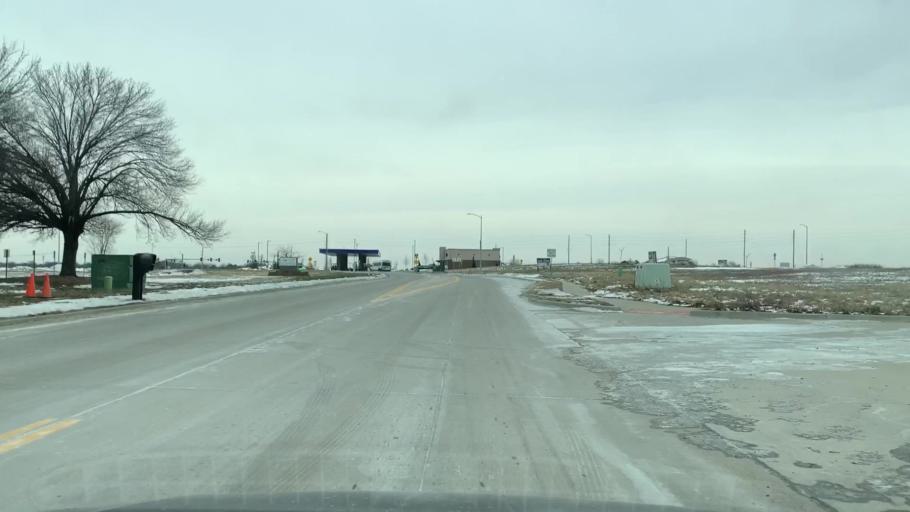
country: US
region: Missouri
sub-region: Jackson County
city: Lees Summit
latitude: 38.9654
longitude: -94.3613
